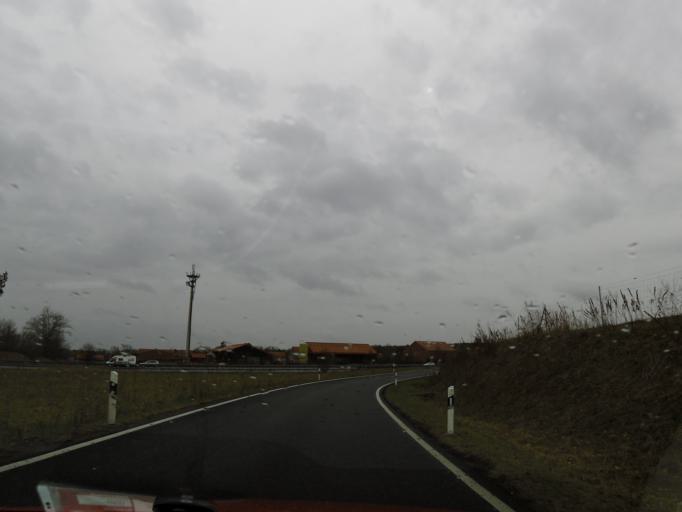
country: DE
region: Brandenburg
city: Rangsdorf
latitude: 52.3081
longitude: 13.4474
